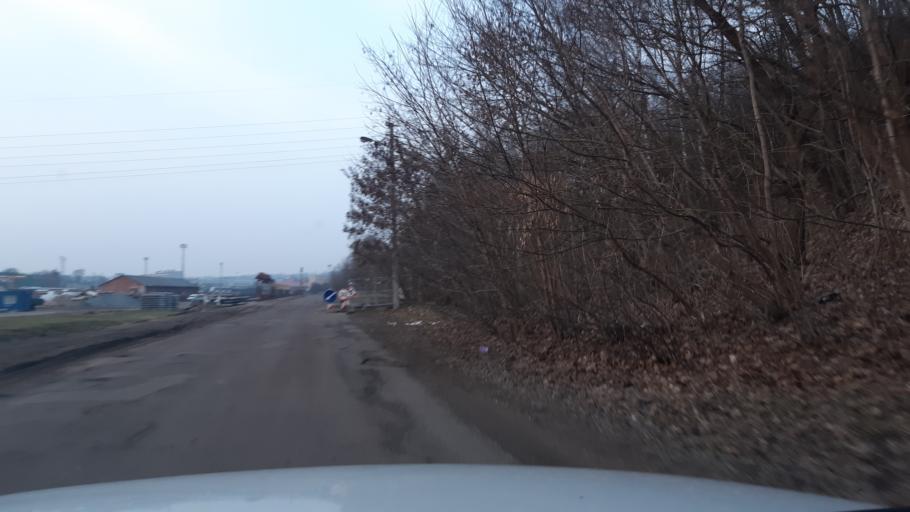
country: LT
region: Kauno apskritis
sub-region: Kaunas
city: Aleksotas
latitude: 54.8790
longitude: 23.9365
